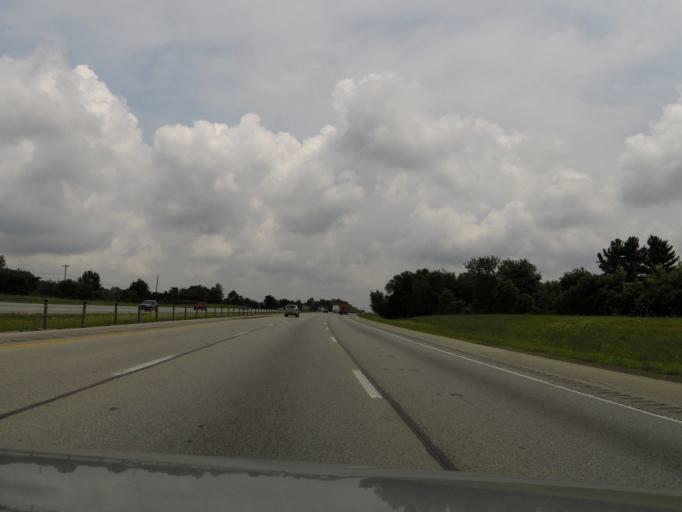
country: US
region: Kentucky
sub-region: Hardin County
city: Elizabethtown
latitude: 37.7286
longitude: -85.8185
